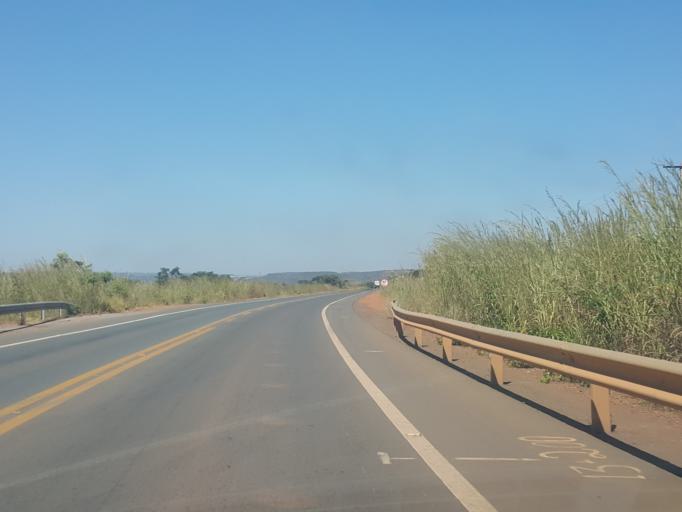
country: BR
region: Goias
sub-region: Luziania
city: Luziania
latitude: -16.0093
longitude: -48.1474
